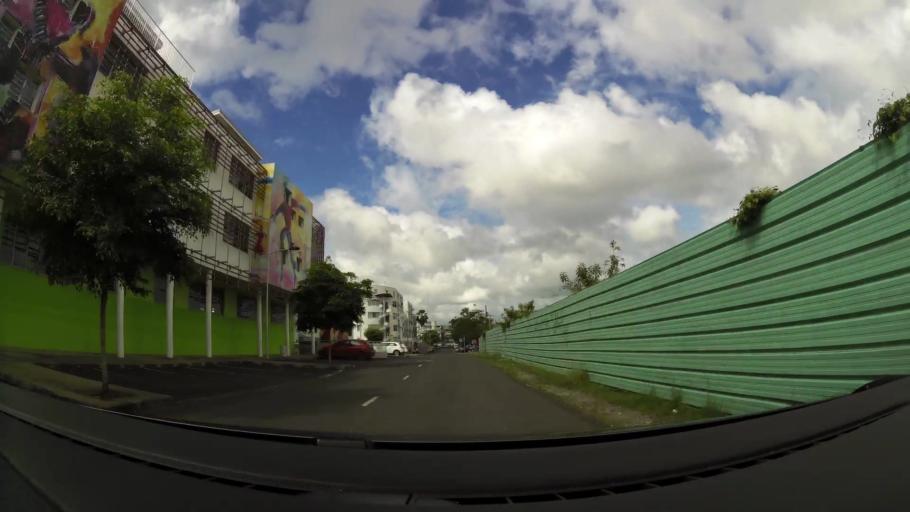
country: GP
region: Guadeloupe
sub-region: Guadeloupe
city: Pointe-a-Pitre
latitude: 16.2453
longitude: -61.5402
